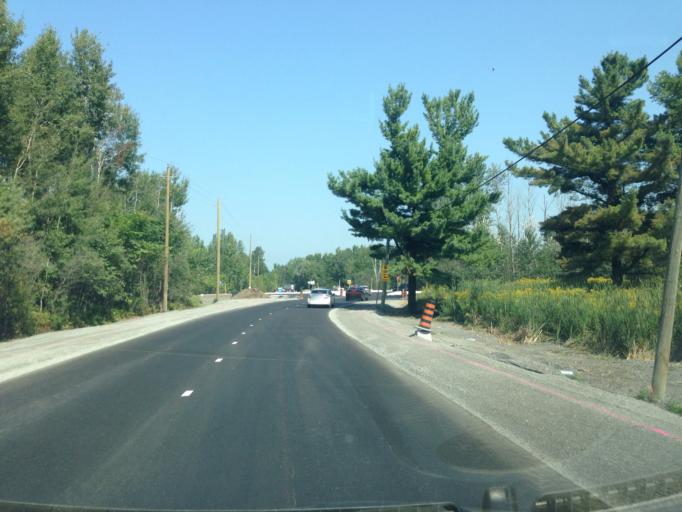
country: CA
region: Ontario
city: Ottawa
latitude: 45.4186
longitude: -75.5670
